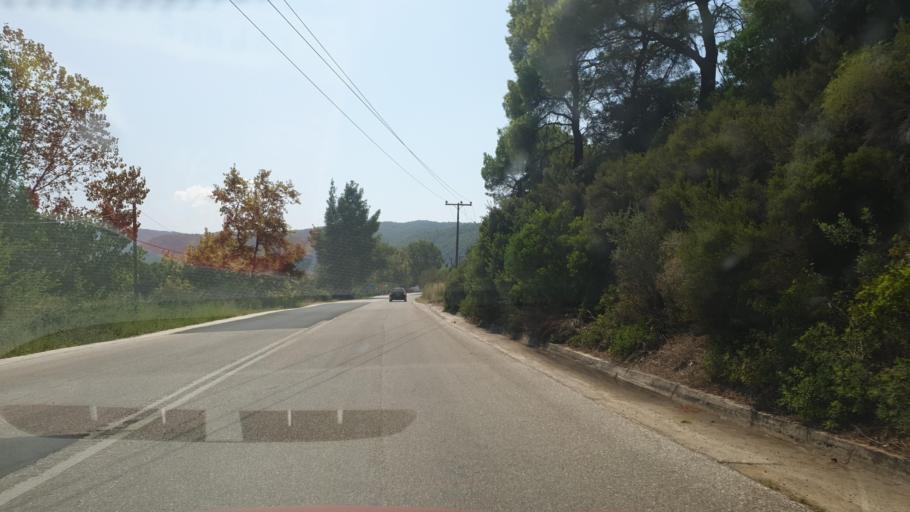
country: GR
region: Central Macedonia
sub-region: Nomos Chalkidikis
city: Agios Nikolaos
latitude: 40.1976
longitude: 23.7672
